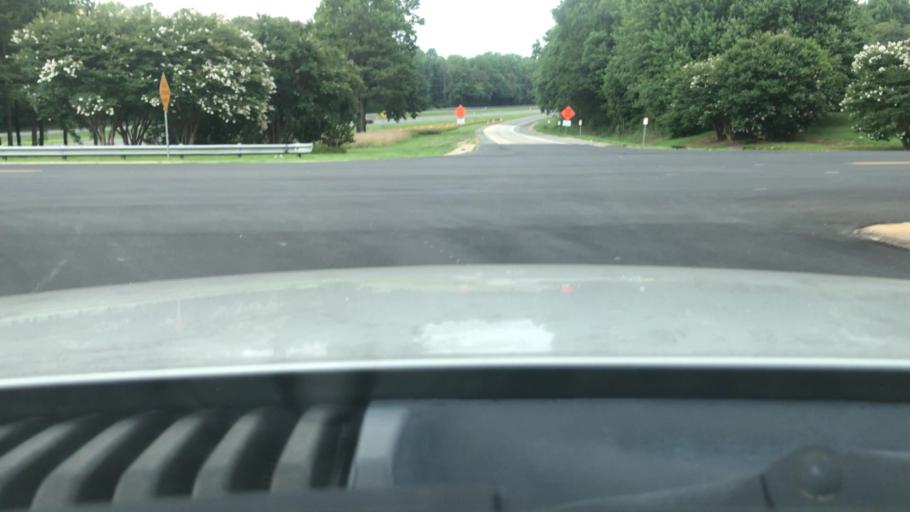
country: US
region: North Carolina
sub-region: Surry County
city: Dobson
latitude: 36.3946
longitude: -80.7862
